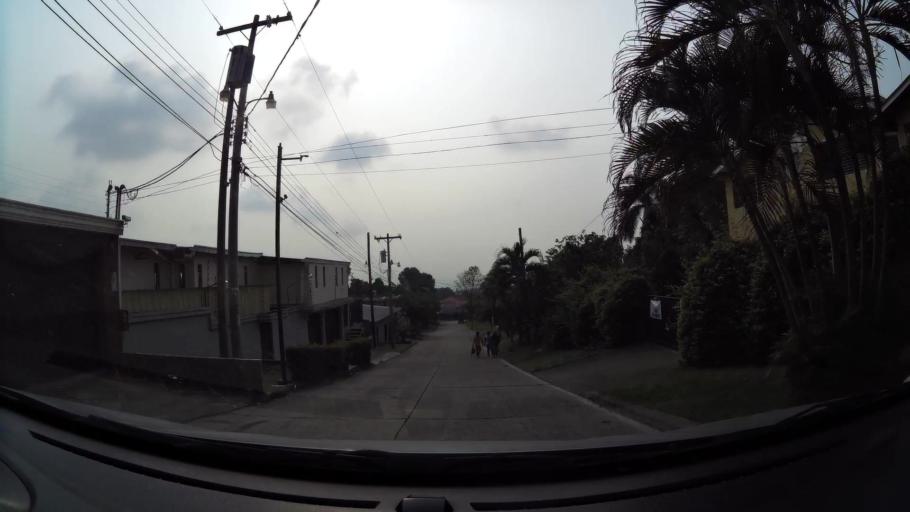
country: HN
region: Cortes
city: Armenta
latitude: 15.4993
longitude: -88.0505
